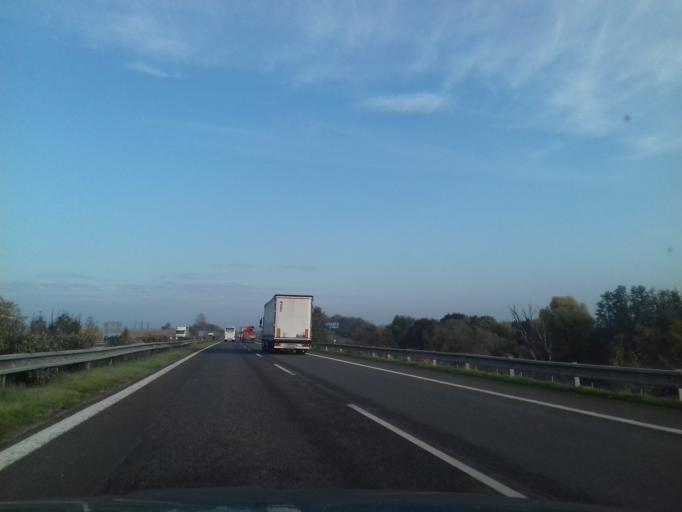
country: SK
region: Bratislavsky
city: Stupava
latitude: 48.2789
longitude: 17.0090
